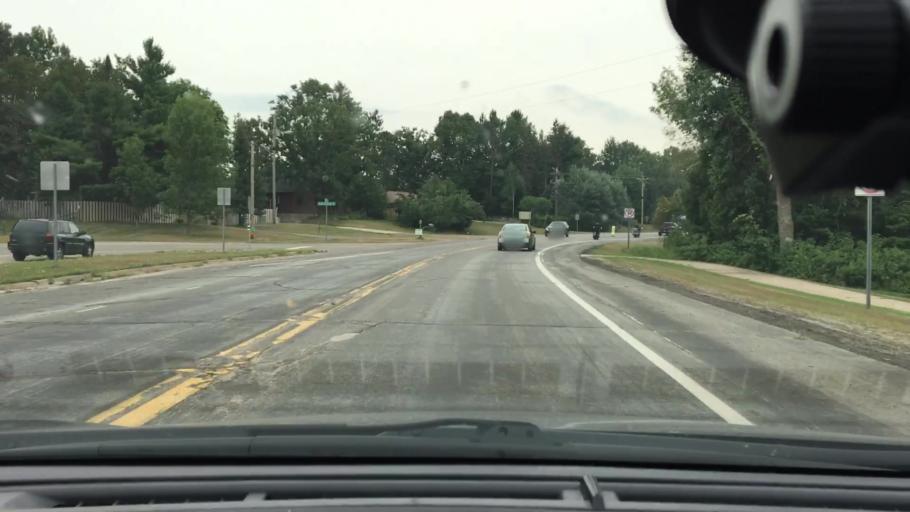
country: US
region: Minnesota
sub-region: Crow Wing County
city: Cross Lake
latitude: 46.8182
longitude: -93.9429
